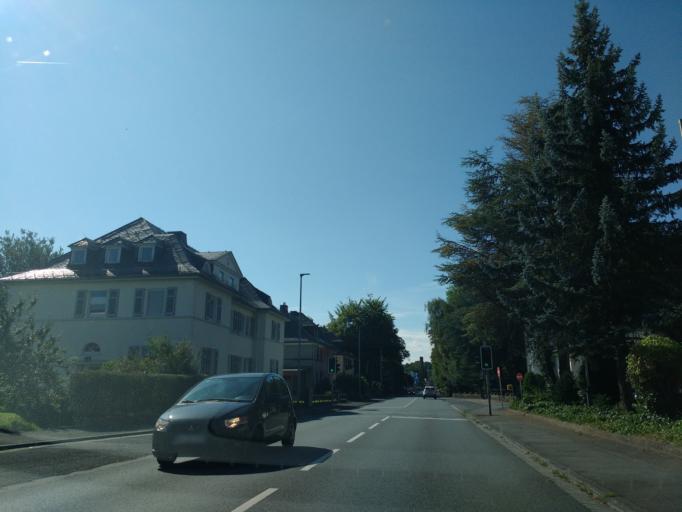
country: DE
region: Hesse
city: Herborn
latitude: 50.6747
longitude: 8.3046
